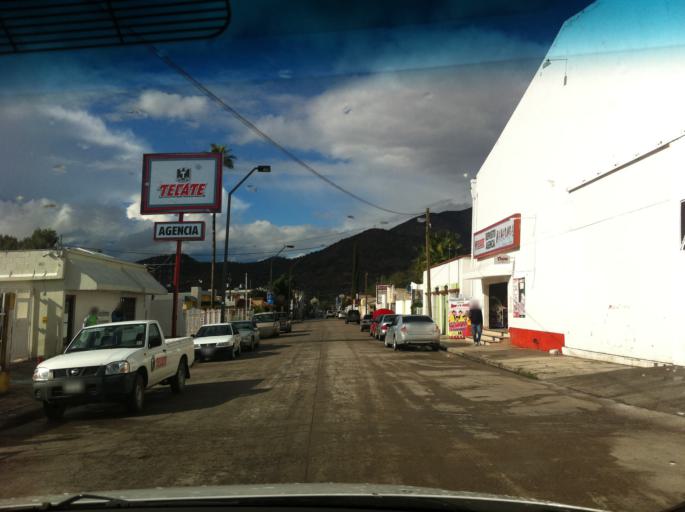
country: MX
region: Sonora
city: Magdalena de Kino
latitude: 30.6262
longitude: -110.9695
